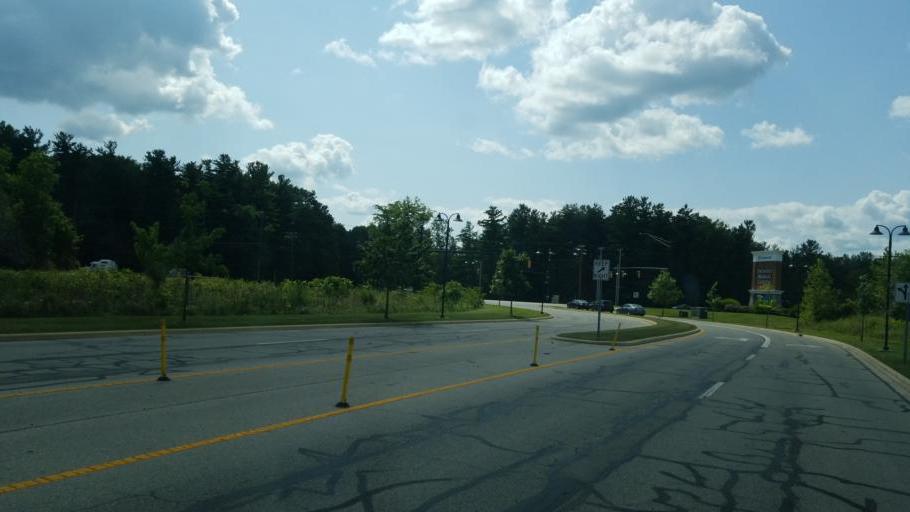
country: US
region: Ohio
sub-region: Delaware County
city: Lewis Center
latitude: 40.2342
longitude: -83.0419
